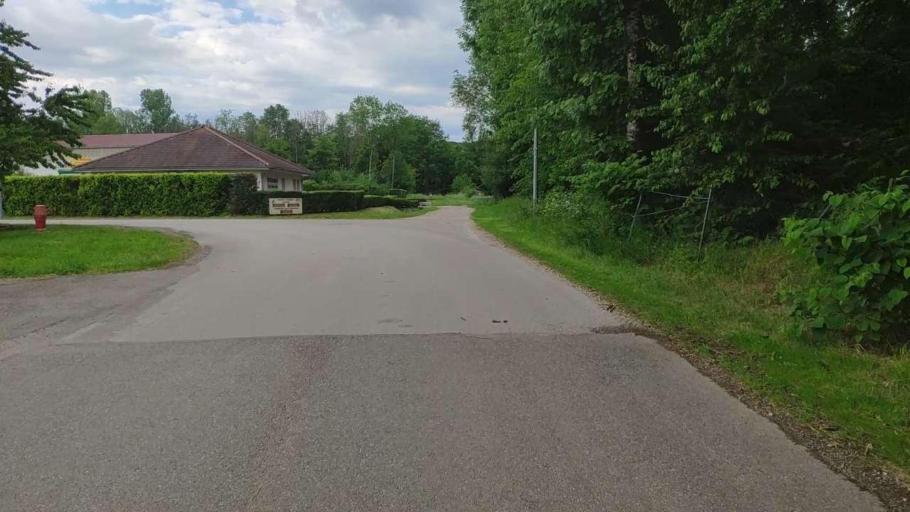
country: FR
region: Franche-Comte
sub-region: Departement du Jura
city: Perrigny
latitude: 46.7582
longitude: 5.5965
